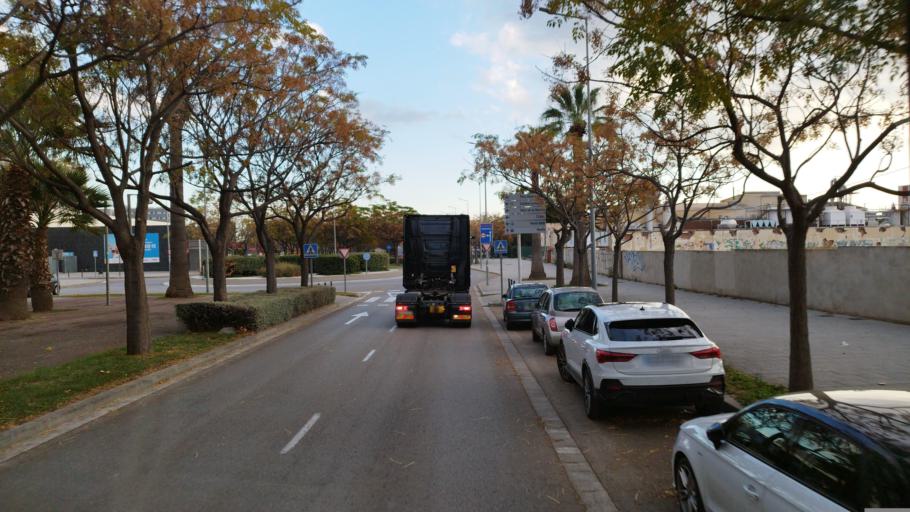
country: ES
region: Catalonia
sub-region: Provincia de Barcelona
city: Viladecans
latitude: 41.3124
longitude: 2.0227
